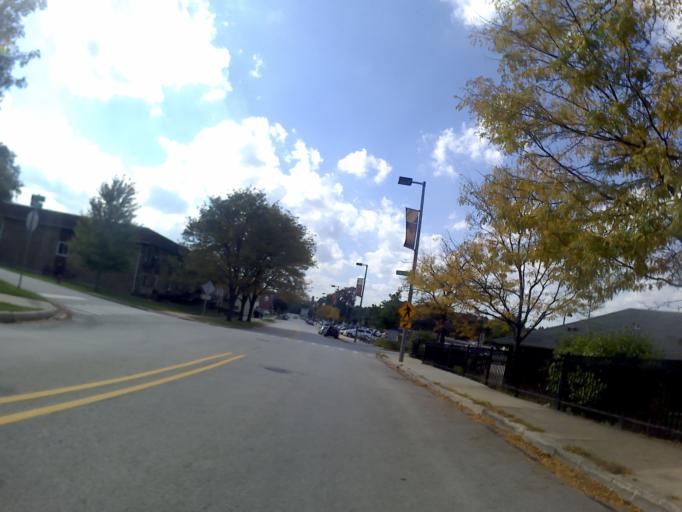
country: US
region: Illinois
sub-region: DuPage County
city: Lisle
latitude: 41.7975
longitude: -88.0721
